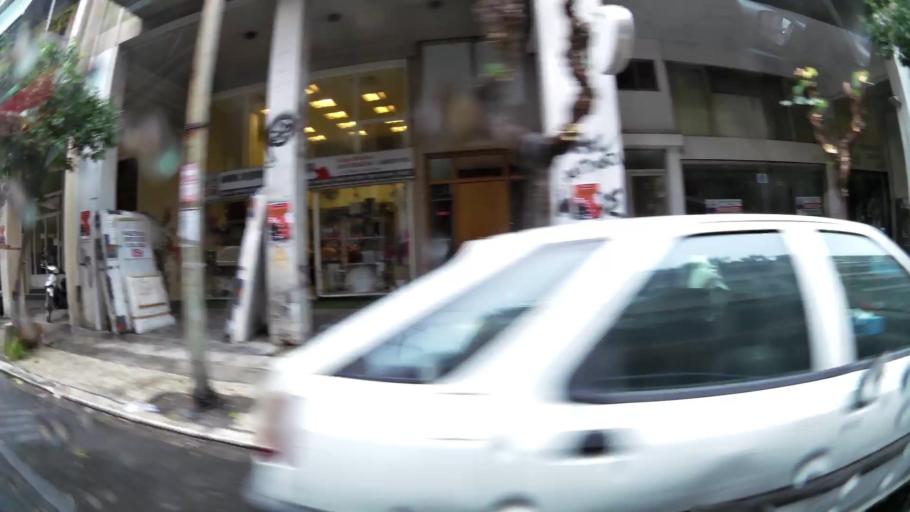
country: GR
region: Attica
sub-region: Nomarchia Athinas
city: Vyronas
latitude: 37.9638
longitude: 23.7505
